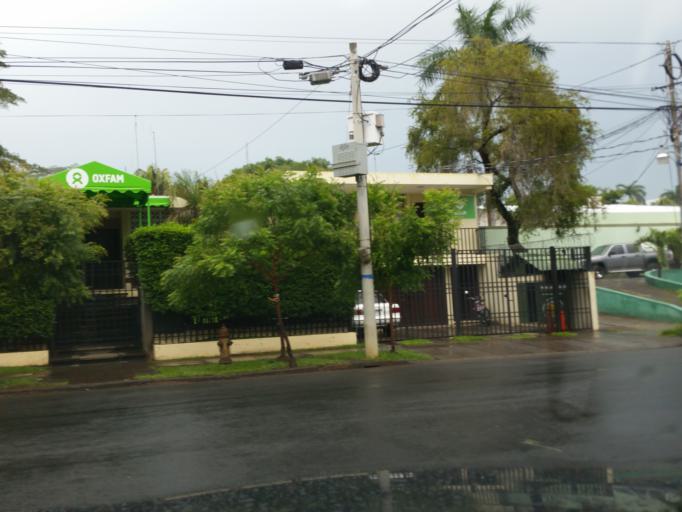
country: NI
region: Managua
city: Managua
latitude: 12.1395
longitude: -86.2768
